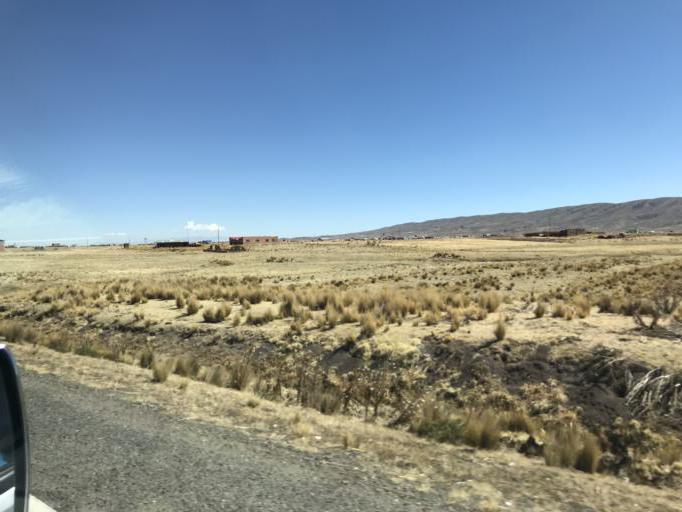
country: BO
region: La Paz
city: Tiahuanaco
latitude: -16.5697
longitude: -68.6649
